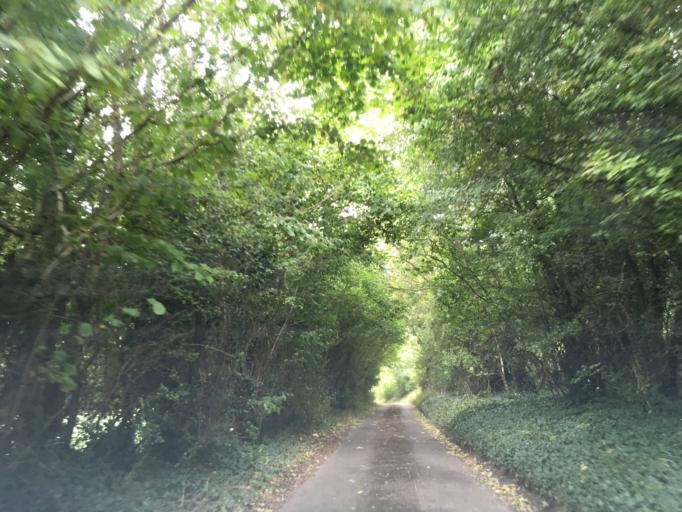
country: GB
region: England
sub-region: South Gloucestershire
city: Tytherington
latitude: 51.5973
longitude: -2.4819
